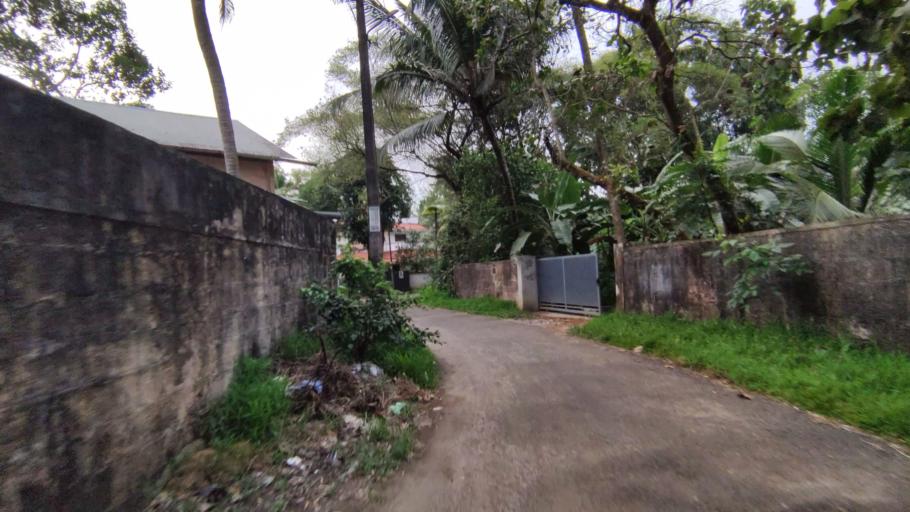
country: IN
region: Kerala
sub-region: Alappuzha
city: Shertallai
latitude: 9.6392
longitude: 76.3630
